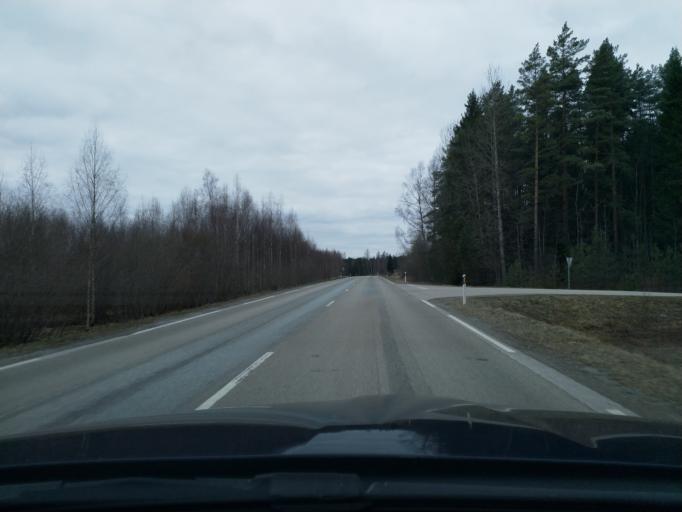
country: LV
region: Kuldigas Rajons
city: Kuldiga
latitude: 56.9528
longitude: 22.2477
